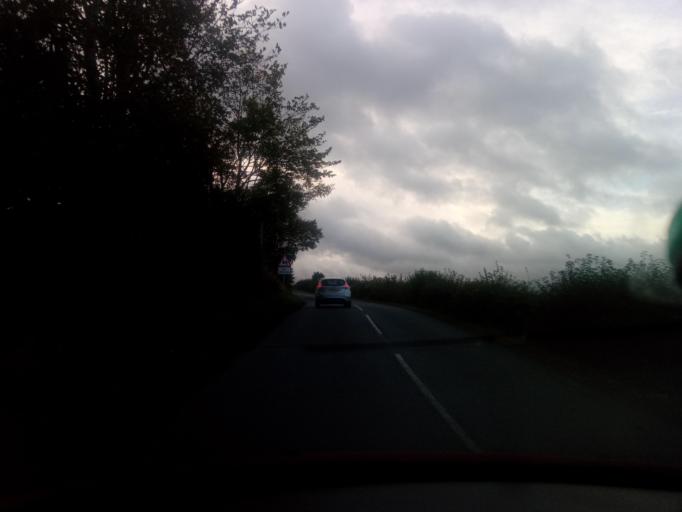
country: GB
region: Scotland
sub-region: The Scottish Borders
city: Jedburgh
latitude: 55.3976
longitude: -2.6509
